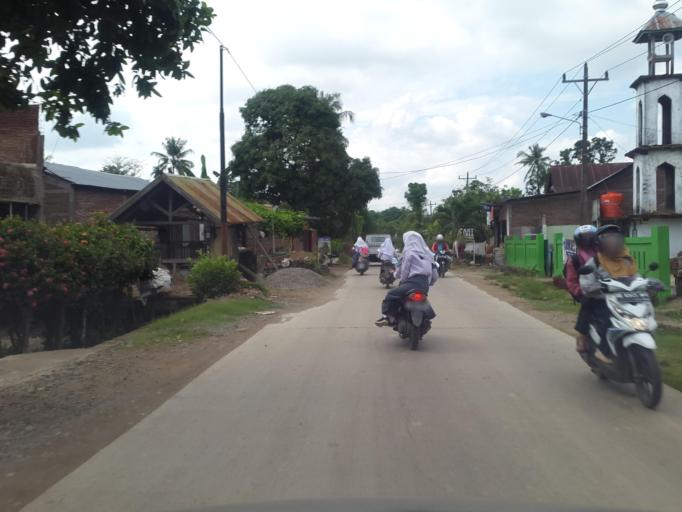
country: ID
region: South Sulawesi
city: Galesong
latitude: -5.3237
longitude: 119.4950
